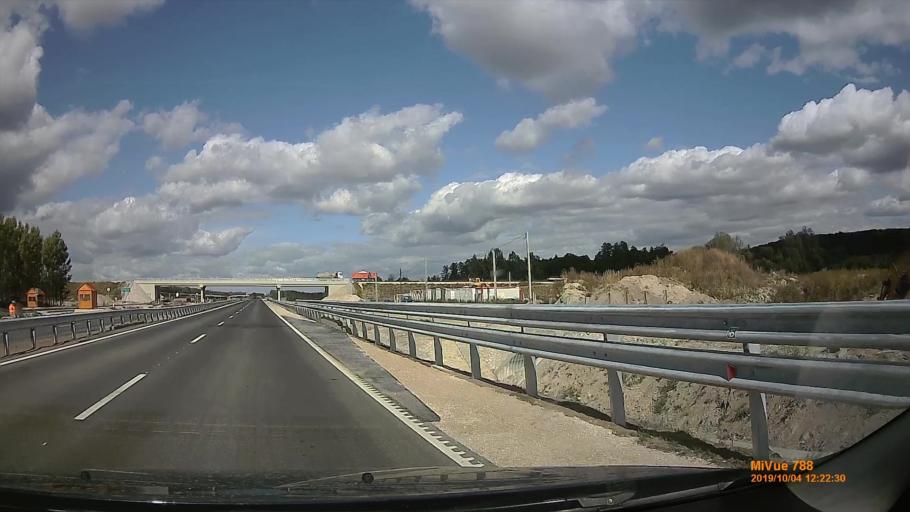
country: HU
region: Somogy
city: Karad
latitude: 46.6222
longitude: 17.7954
